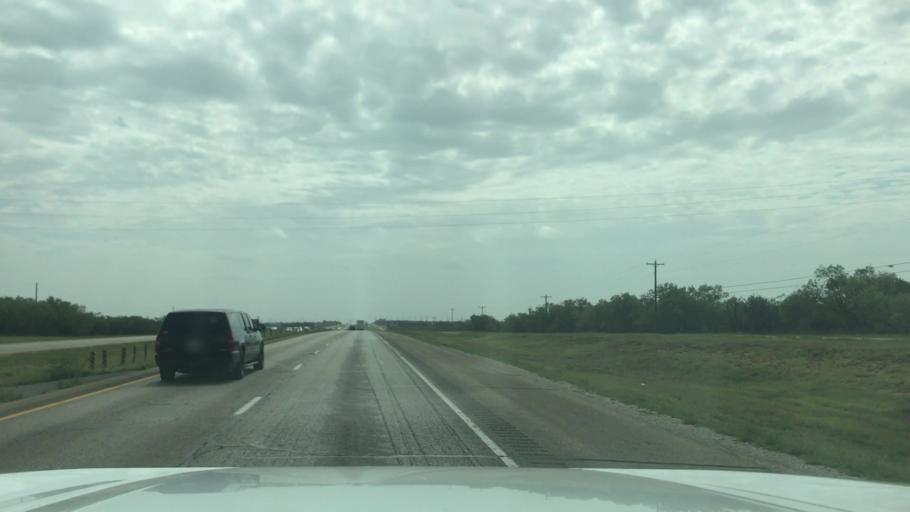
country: US
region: Texas
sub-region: Callahan County
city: Clyde
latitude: 32.4211
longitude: -99.5428
